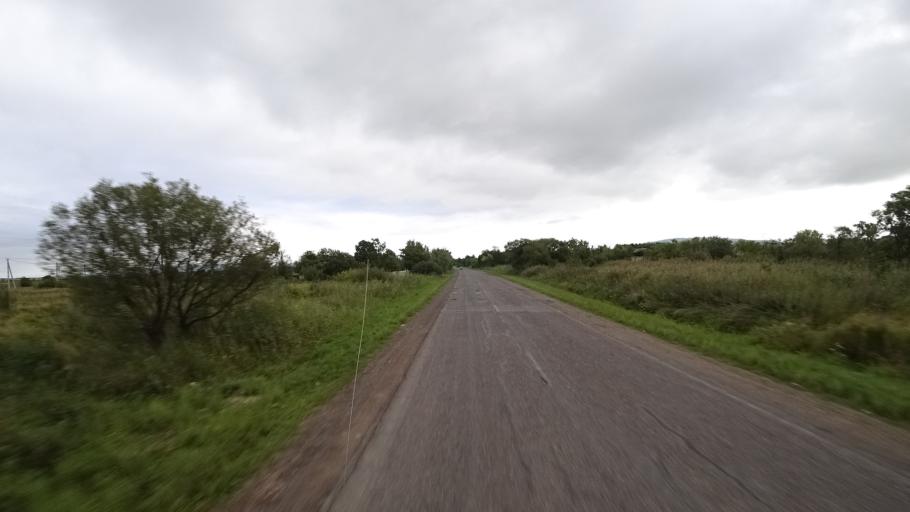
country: RU
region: Primorskiy
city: Chernigovka
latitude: 44.3560
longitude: 132.5625
